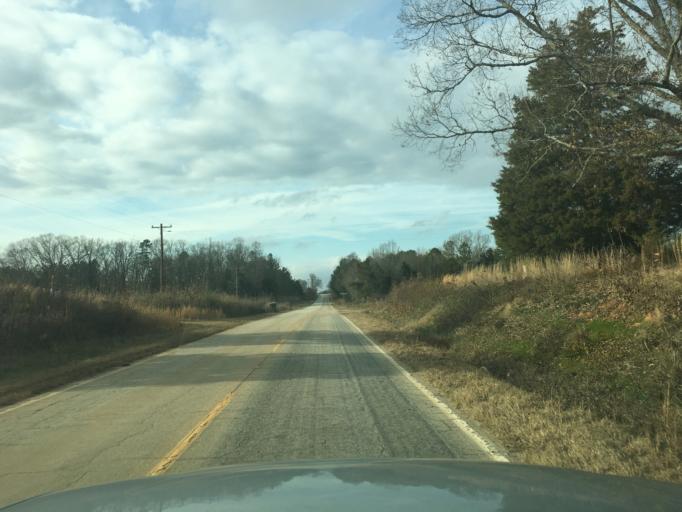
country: US
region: South Carolina
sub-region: Abbeville County
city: Due West
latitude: 34.3406
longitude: -82.4910
